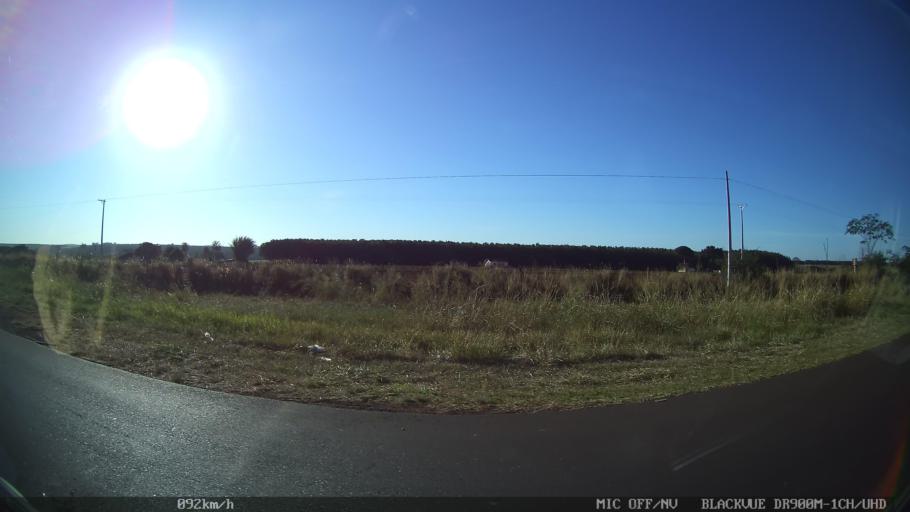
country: BR
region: Sao Paulo
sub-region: Guapiacu
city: Guapiacu
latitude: -20.7513
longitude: -49.1387
